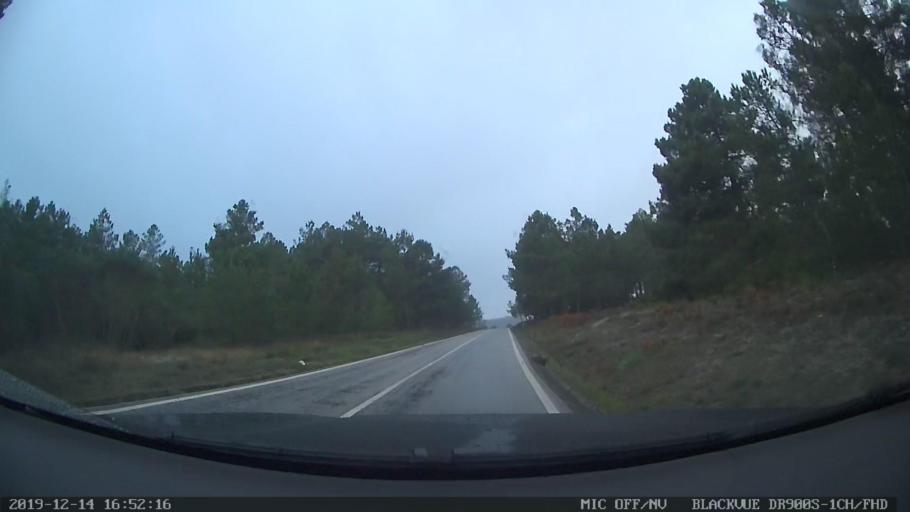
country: PT
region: Vila Real
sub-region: Murca
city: Murca
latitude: 41.4264
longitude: -7.5072
